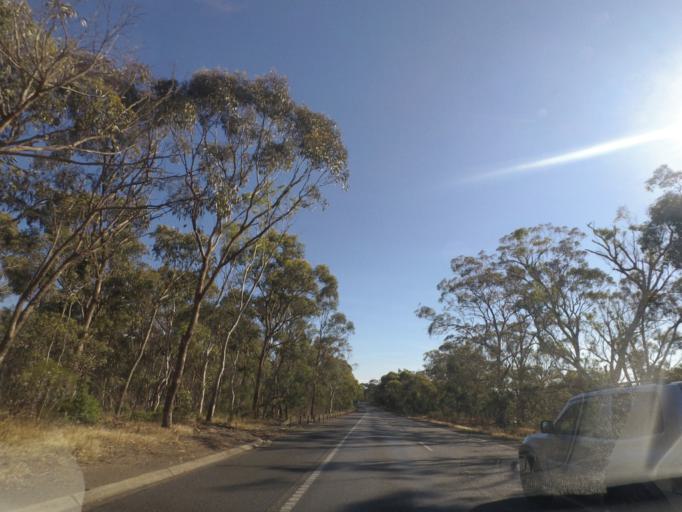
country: AU
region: Victoria
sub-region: Murrindindi
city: Kinglake West
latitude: -37.1759
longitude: 145.0723
